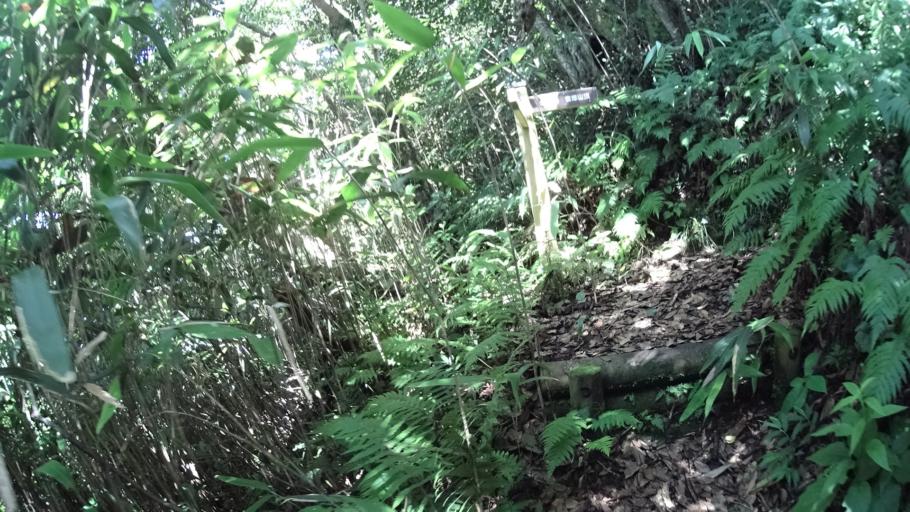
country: JP
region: Shizuoka
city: Shimoda
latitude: 34.5172
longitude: 139.2772
